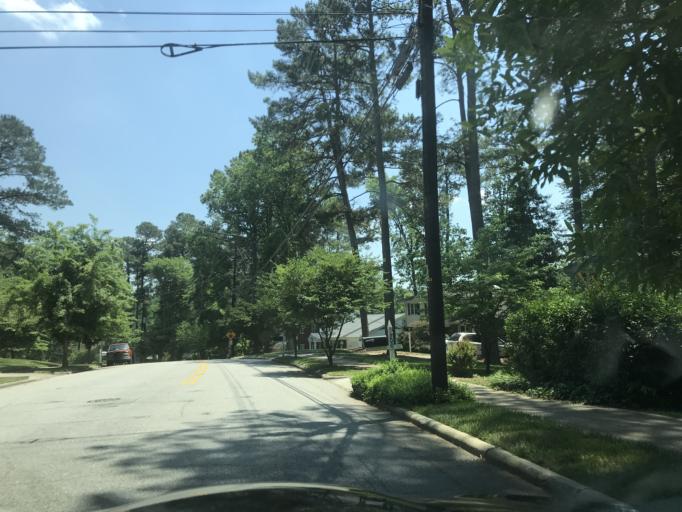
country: US
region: North Carolina
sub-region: Wake County
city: West Raleigh
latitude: 35.8372
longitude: -78.6291
